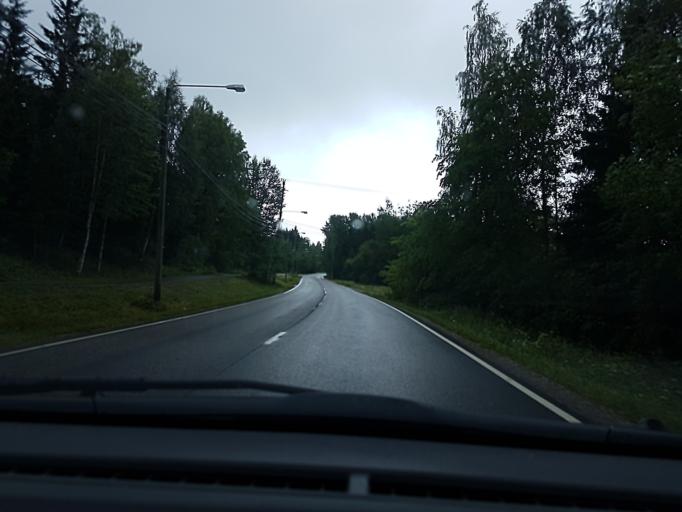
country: FI
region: Uusimaa
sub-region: Helsinki
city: Pornainen
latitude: 60.4689
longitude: 25.3844
